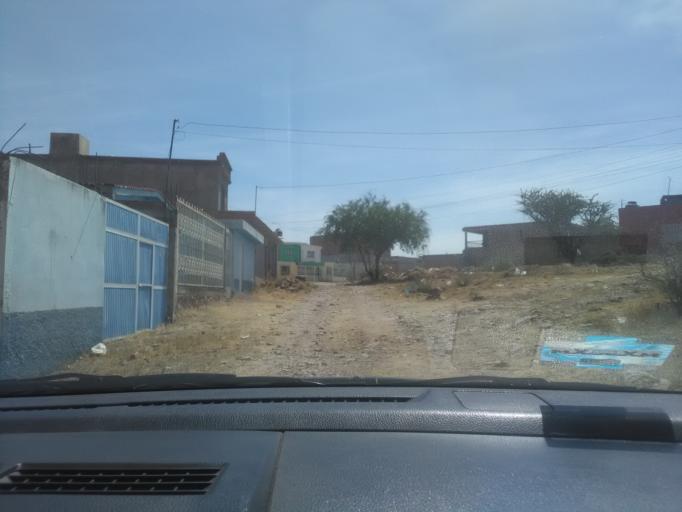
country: MX
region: Durango
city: Victoria de Durango
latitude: 24.0486
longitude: -104.6995
